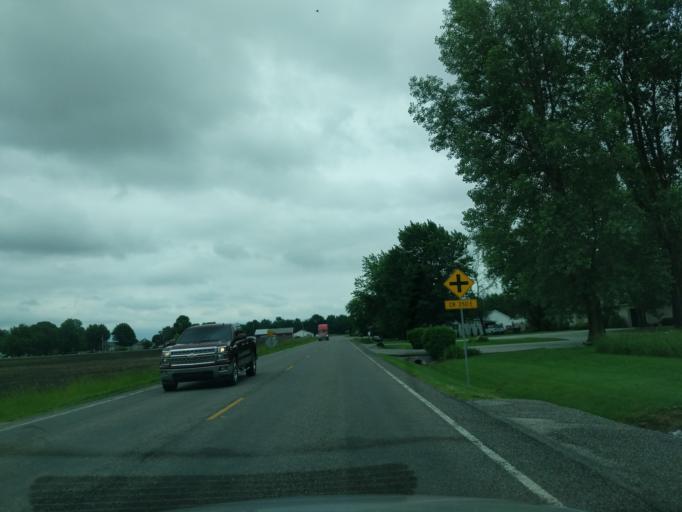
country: US
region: Indiana
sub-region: Tipton County
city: Tipton
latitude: 40.2852
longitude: -85.9510
